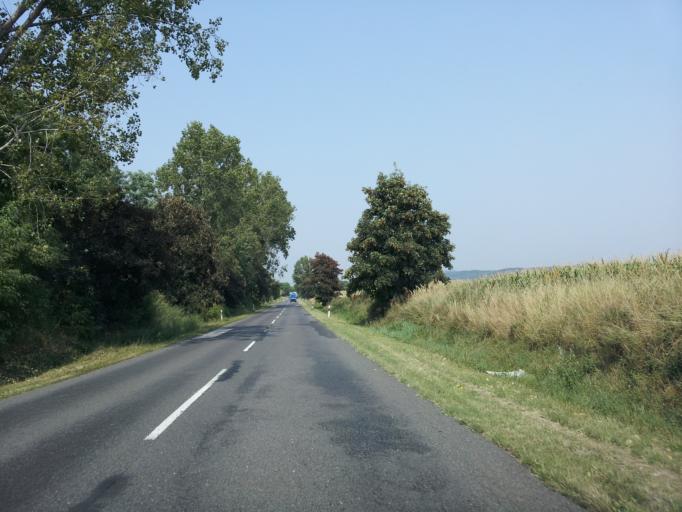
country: HU
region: Gyor-Moson-Sopron
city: Pannonhalma
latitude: 47.4873
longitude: 17.7836
